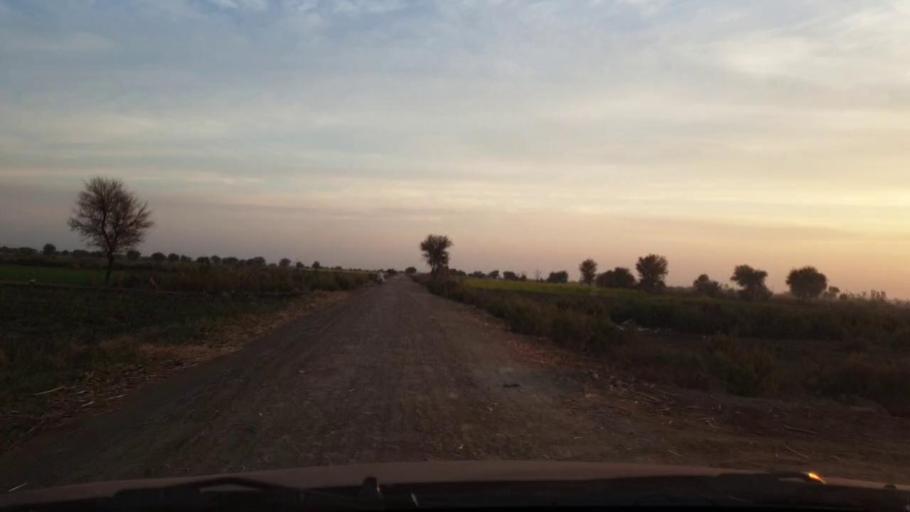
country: PK
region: Sindh
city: Sinjhoro
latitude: 26.0982
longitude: 68.7969
